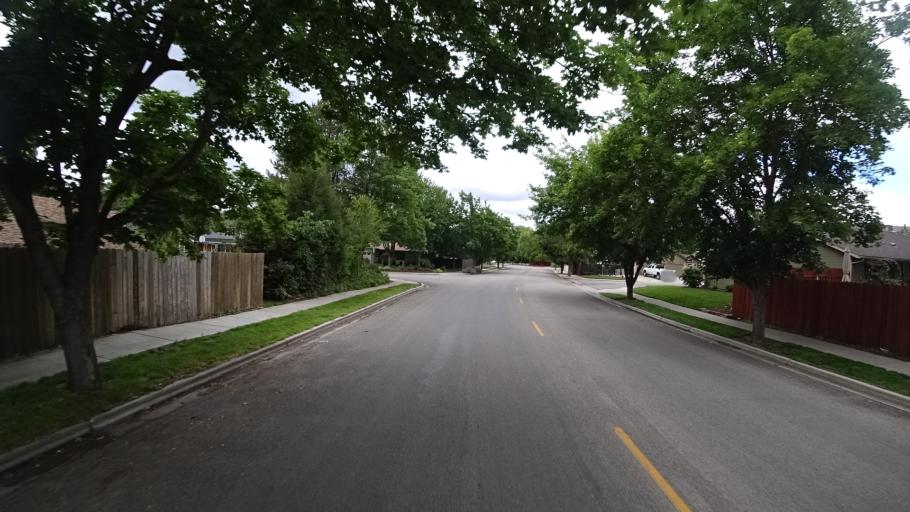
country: US
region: Idaho
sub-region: Ada County
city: Garden City
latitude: 43.6602
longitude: -116.2511
